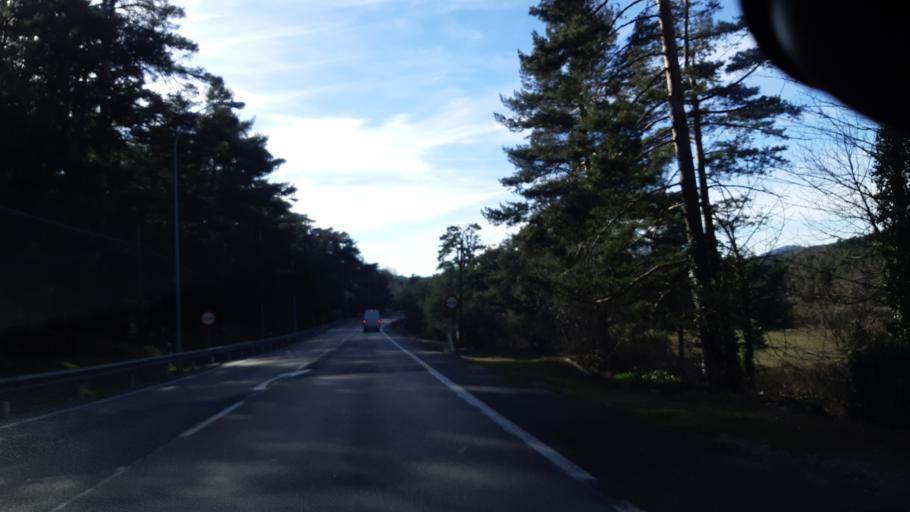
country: ES
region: Madrid
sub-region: Provincia de Madrid
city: Guadarrama
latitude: 40.7107
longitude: -4.1744
